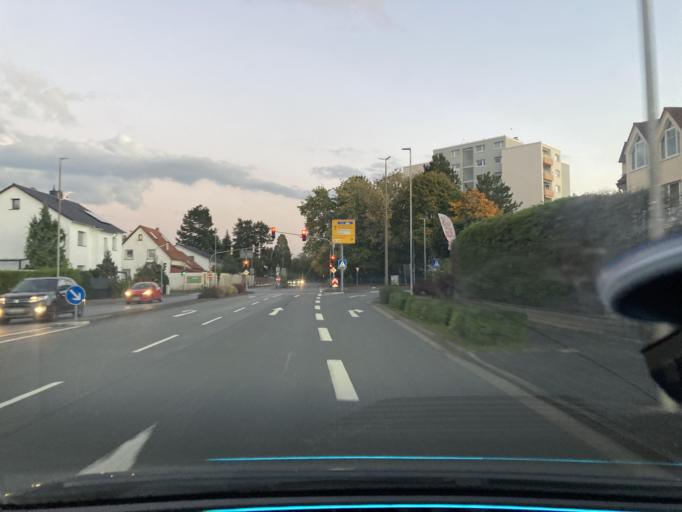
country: DE
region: Hesse
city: Heusenstamm
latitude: 50.0555
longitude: 8.7963
